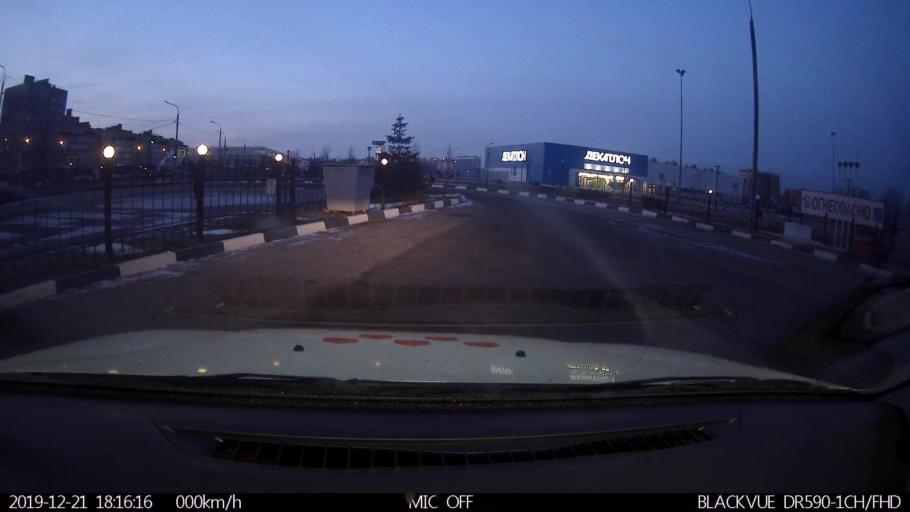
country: RU
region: Nizjnij Novgorod
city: Nizhniy Novgorod
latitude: 56.3354
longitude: 43.9560
